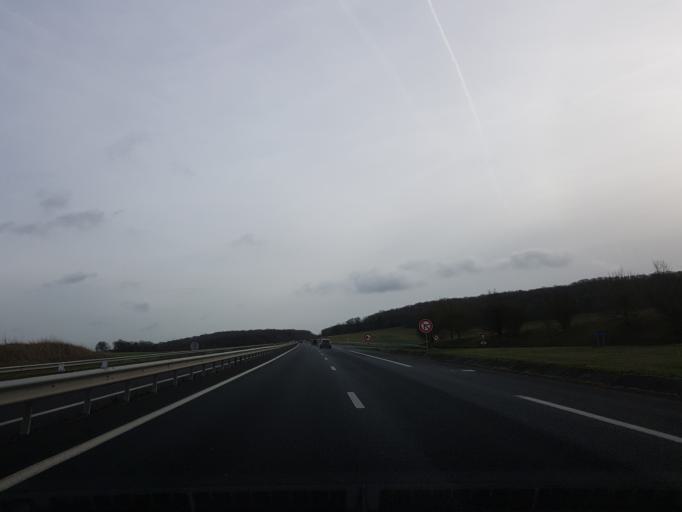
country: FR
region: Bourgogne
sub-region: Departement de l'Yonne
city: Soucy
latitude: 48.2463
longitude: 3.3502
